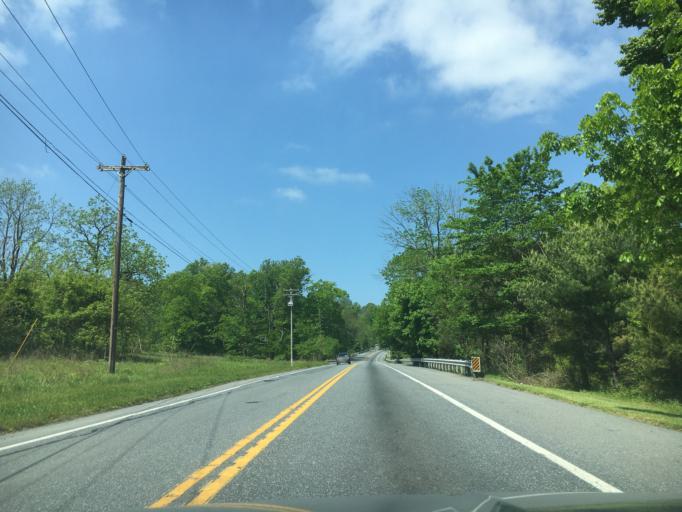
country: US
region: Pennsylvania
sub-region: Berks County
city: New Berlinville
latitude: 40.3623
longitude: -75.6856
